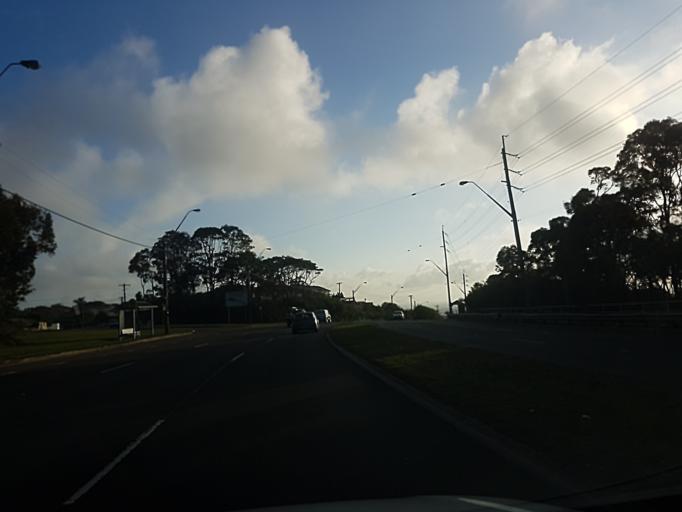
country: AU
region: New South Wales
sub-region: Warringah
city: Brookvale
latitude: -33.7546
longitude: 151.2649
